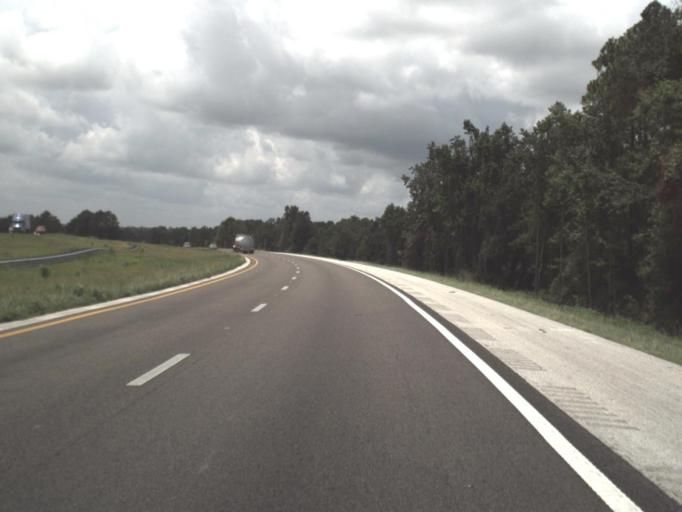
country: US
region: Florida
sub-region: Pasco County
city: San Antonio
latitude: 28.4004
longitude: -82.3148
